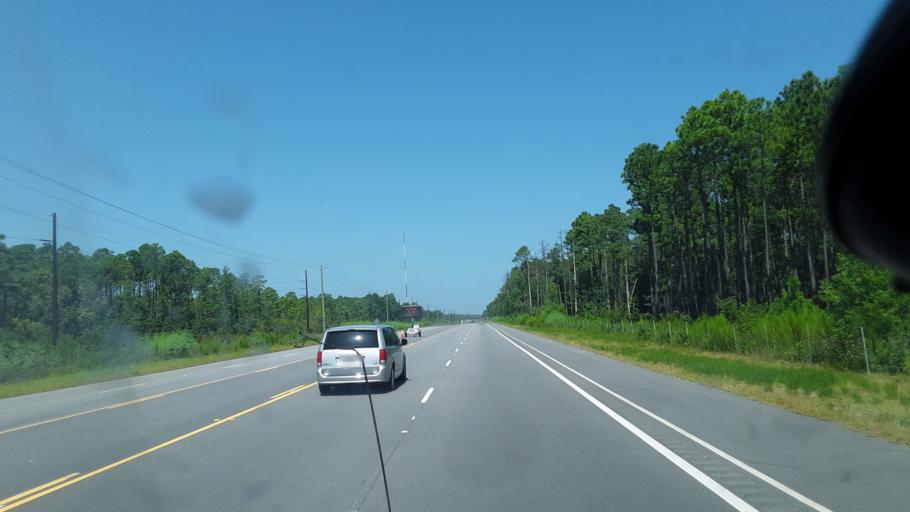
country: US
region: South Carolina
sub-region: Horry County
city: Myrtle Beach
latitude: 33.7732
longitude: -78.8699
